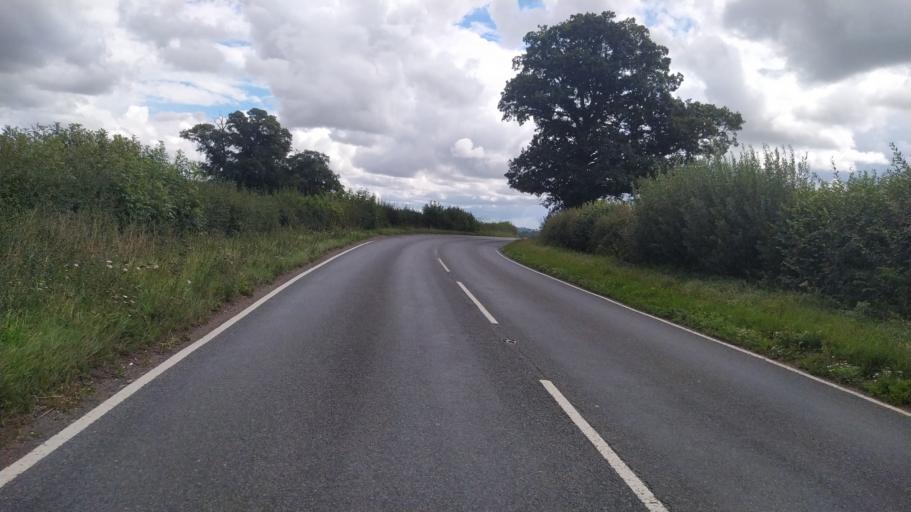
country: GB
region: England
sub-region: Dorset
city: Manston
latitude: 50.9111
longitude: -2.2676
